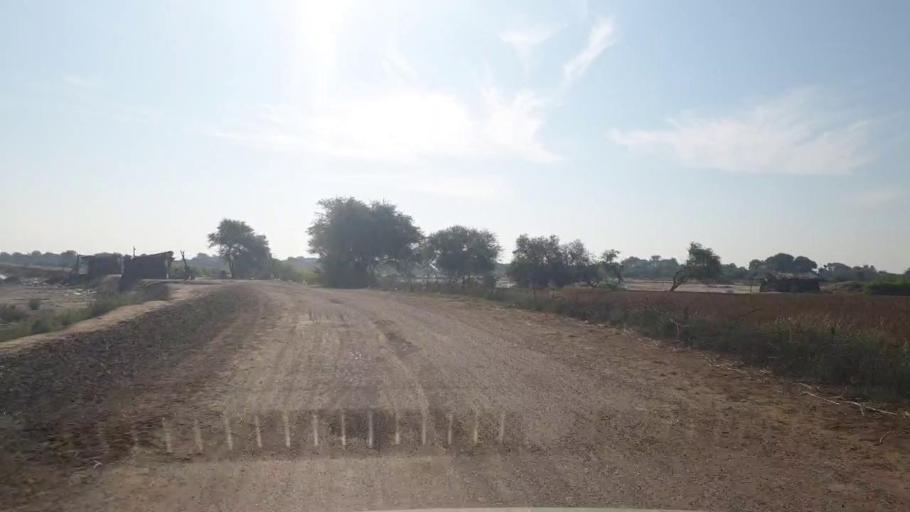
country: PK
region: Sindh
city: Rajo Khanani
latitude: 24.9725
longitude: 68.7868
